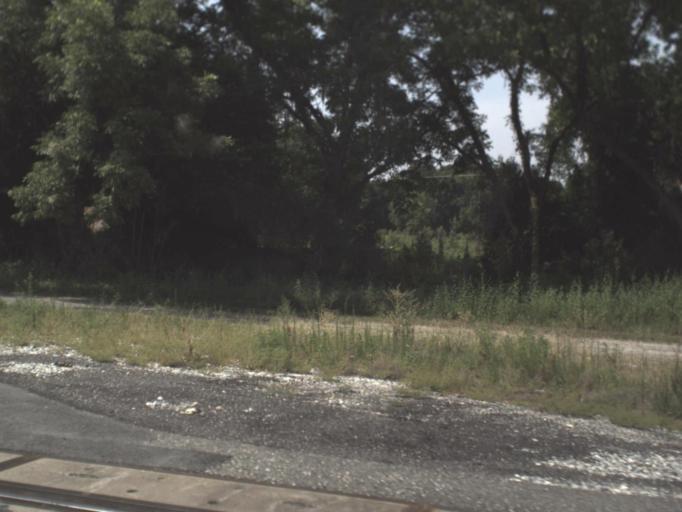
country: US
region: Florida
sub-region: Hamilton County
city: Jasper
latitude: 30.5486
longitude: -82.9782
